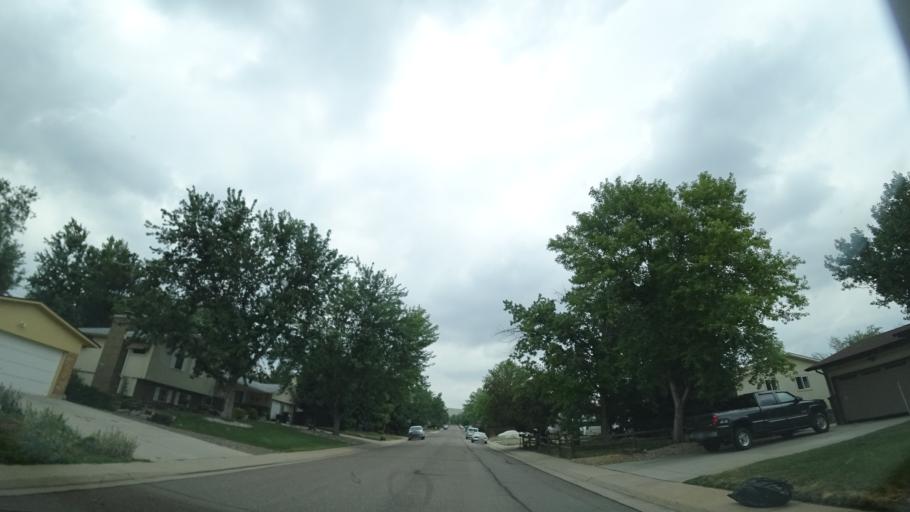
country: US
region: Colorado
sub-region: Jefferson County
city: West Pleasant View
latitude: 39.7095
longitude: -105.1513
